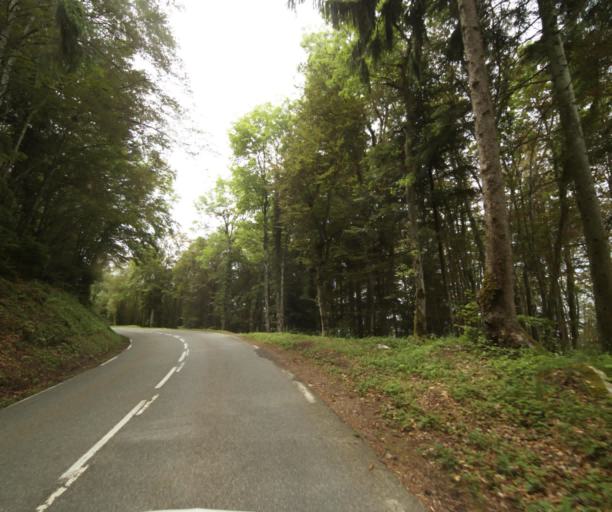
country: FR
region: Rhone-Alpes
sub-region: Departement de la Haute-Savoie
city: Perrignier
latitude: 46.2795
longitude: 6.4575
